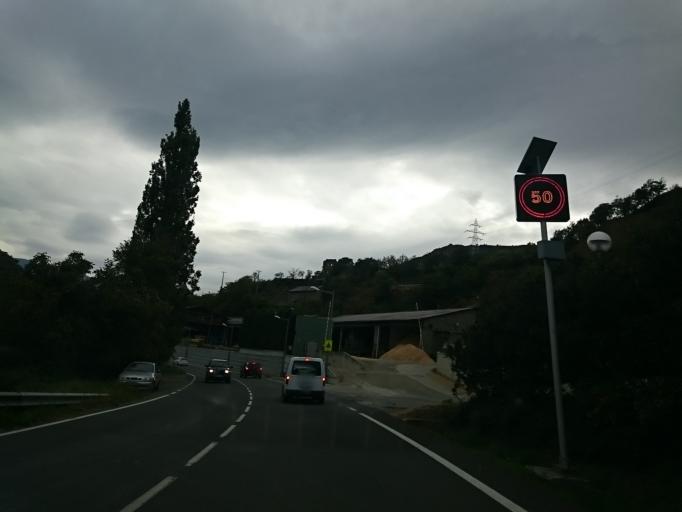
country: ES
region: Catalonia
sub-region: Provincia de Lleida
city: Sort
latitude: 42.4469
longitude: 1.1358
